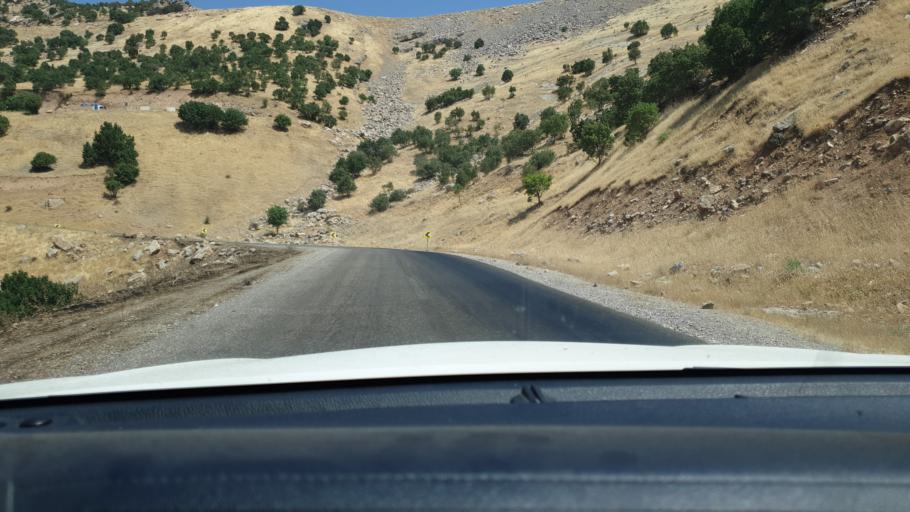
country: IQ
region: Arbil
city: Nahiyat Hiran
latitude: 36.3042
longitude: 44.4267
